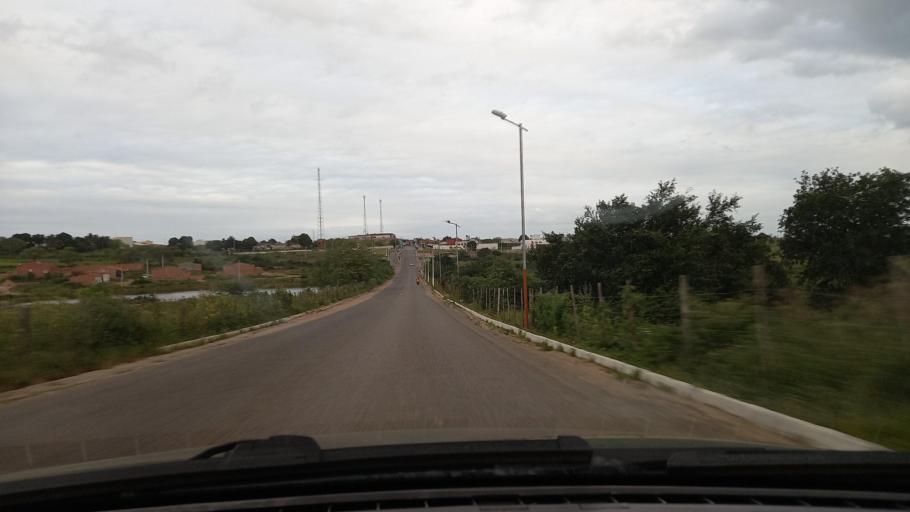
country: BR
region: Sergipe
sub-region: Caninde De Sao Francisco
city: Caninde de Sao Francisco
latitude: -9.6018
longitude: -37.7648
